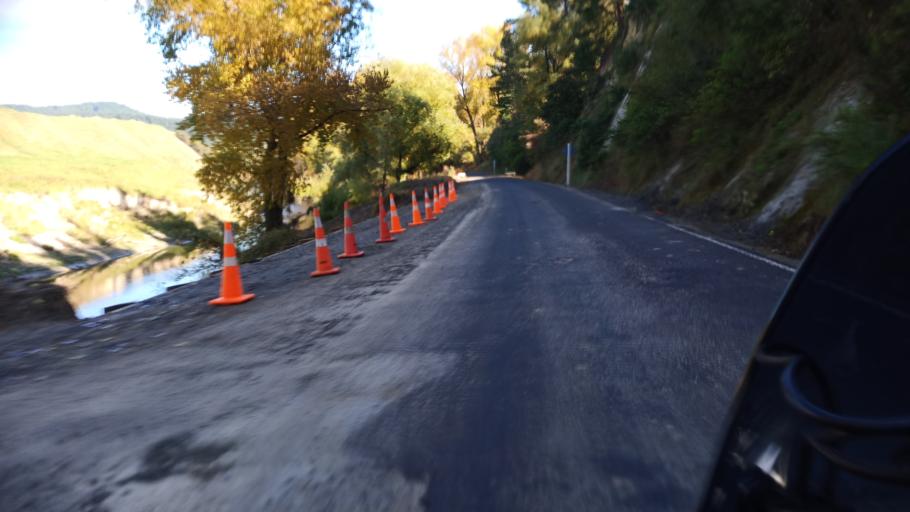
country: NZ
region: Hawke's Bay
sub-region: Wairoa District
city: Wairoa
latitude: -38.9206
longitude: 177.2566
